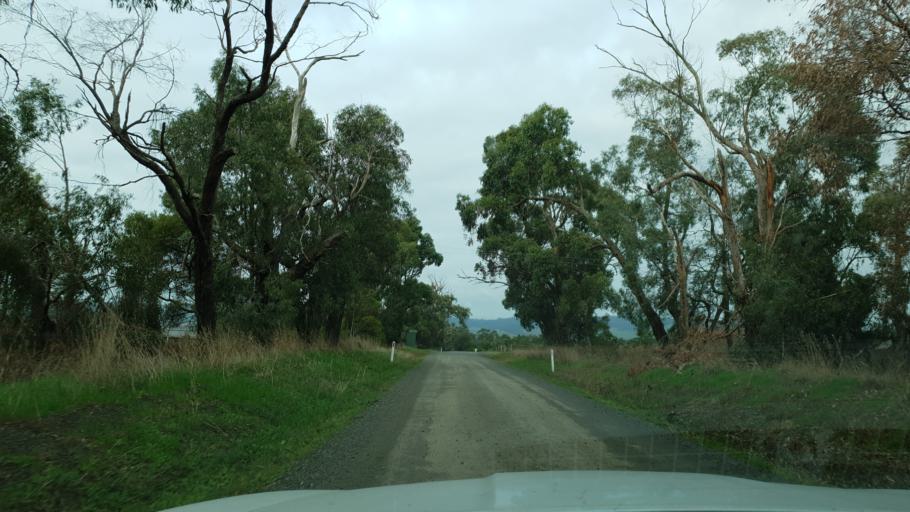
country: AU
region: Victoria
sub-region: Latrobe
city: Moe
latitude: -38.1727
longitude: 146.1310
